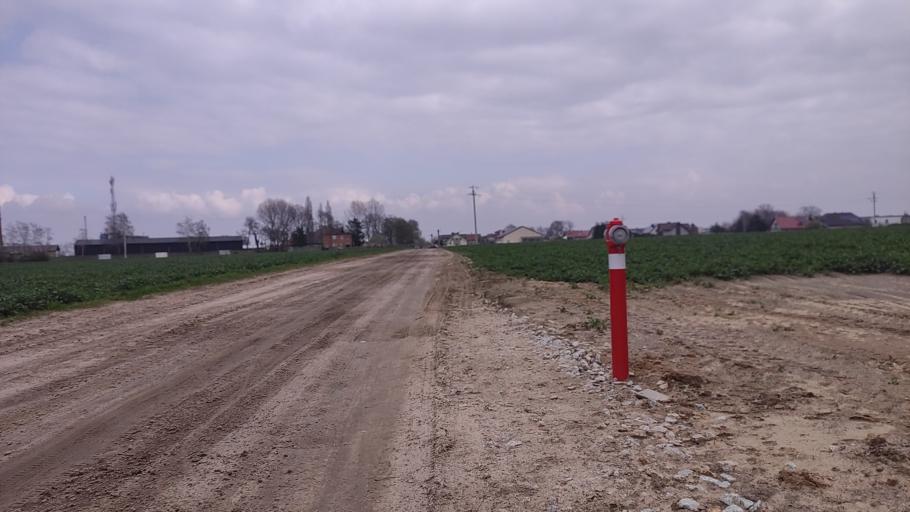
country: PL
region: Greater Poland Voivodeship
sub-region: Powiat poznanski
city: Swarzedz
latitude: 52.4026
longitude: 17.1546
